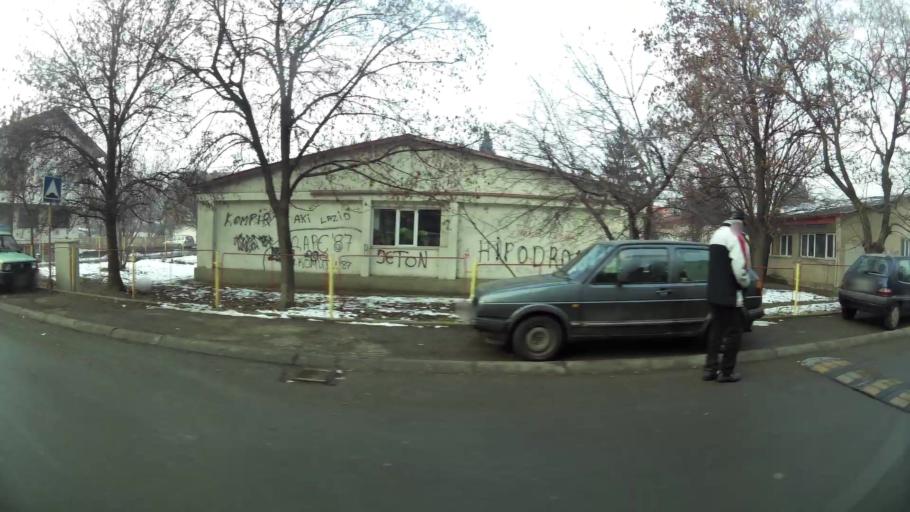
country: MK
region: Kisela Voda
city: Kisela Voda
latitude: 41.9946
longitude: 21.5088
